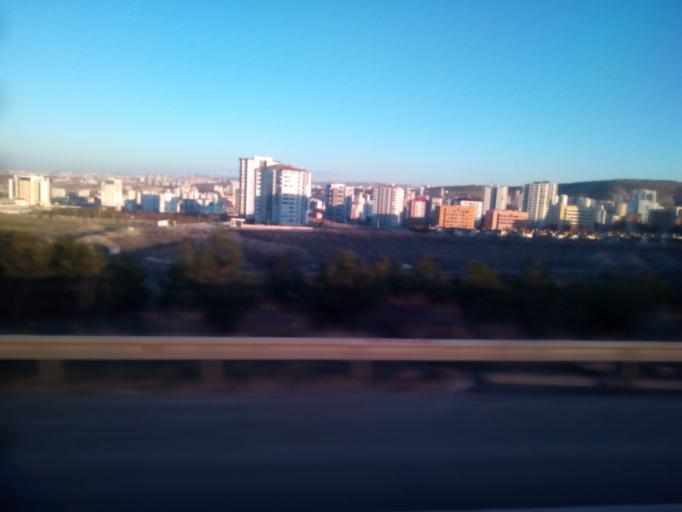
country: TR
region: Ankara
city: Etimesgut
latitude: 39.9038
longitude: 32.6253
